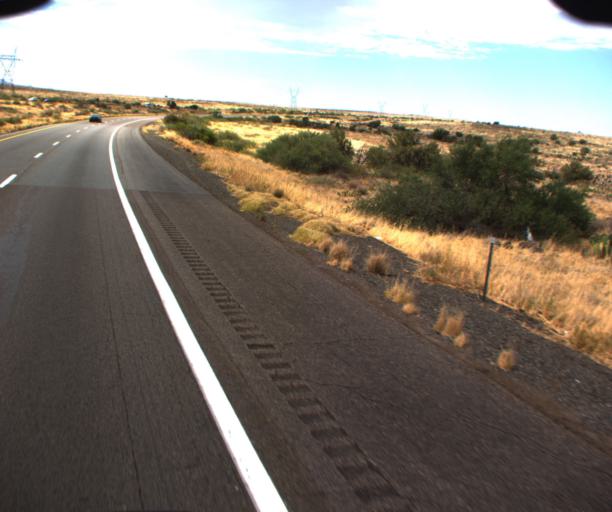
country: US
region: Arizona
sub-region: Yavapai County
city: Cordes Lakes
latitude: 34.2216
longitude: -112.1120
